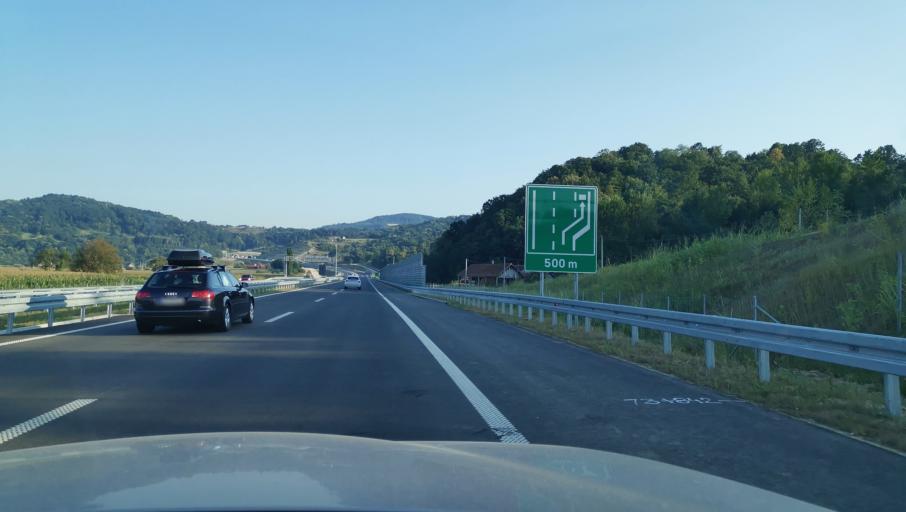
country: RS
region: Central Serbia
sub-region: Kolubarski Okrug
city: Ljig
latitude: 44.2263
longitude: 20.2540
